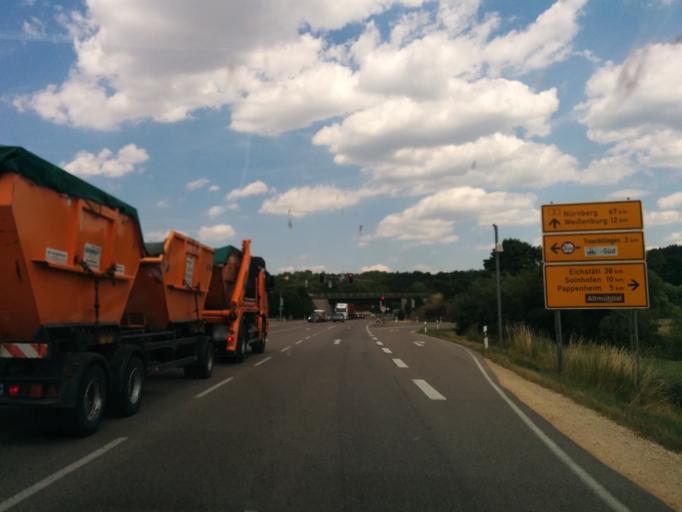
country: DE
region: Bavaria
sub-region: Regierungsbezirk Mittelfranken
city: Treuchtlingen
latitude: 48.9376
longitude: 10.9247
